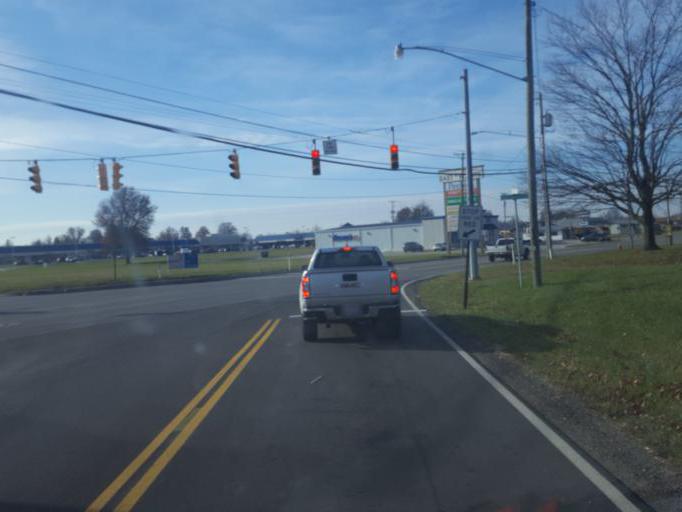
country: US
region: Ohio
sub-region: Crawford County
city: Bucyrus
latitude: 40.8127
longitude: -82.9464
